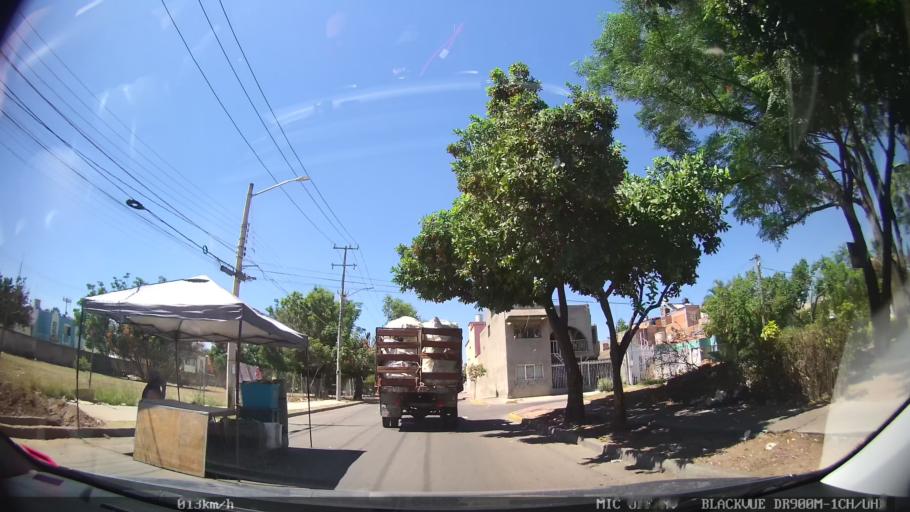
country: MX
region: Jalisco
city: Tlaquepaque
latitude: 20.6653
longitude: -103.2850
